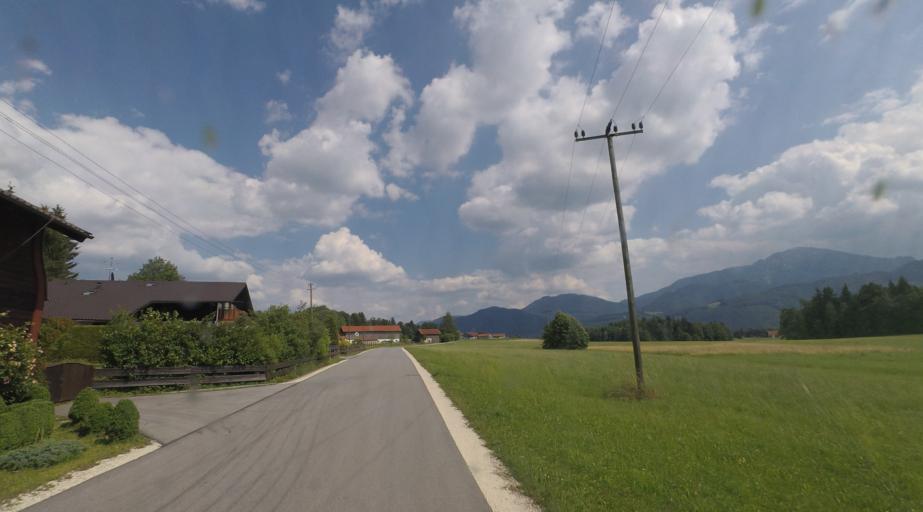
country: DE
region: Bavaria
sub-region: Upper Bavaria
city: Grabenstatt
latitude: 47.8251
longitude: 12.5498
